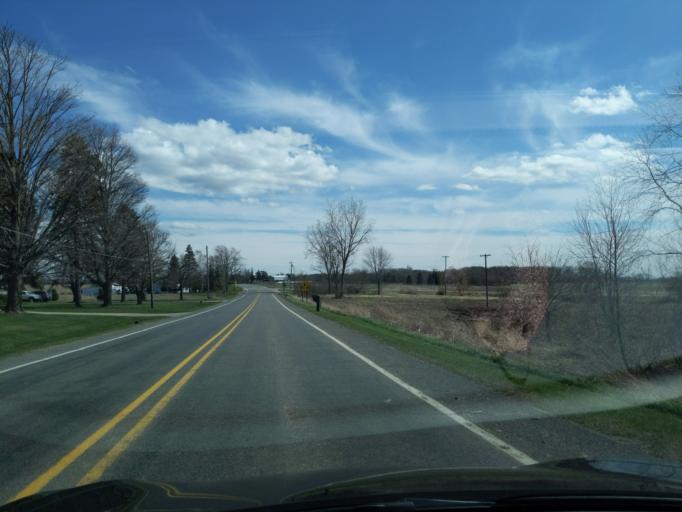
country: US
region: Michigan
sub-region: Ingham County
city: Mason
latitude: 42.5693
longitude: -84.4153
